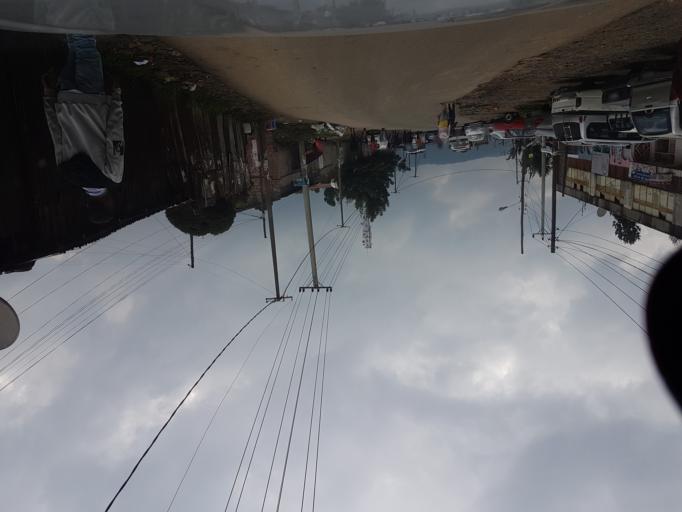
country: ET
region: Adis Abeba
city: Addis Ababa
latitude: 9.0228
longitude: 38.7668
